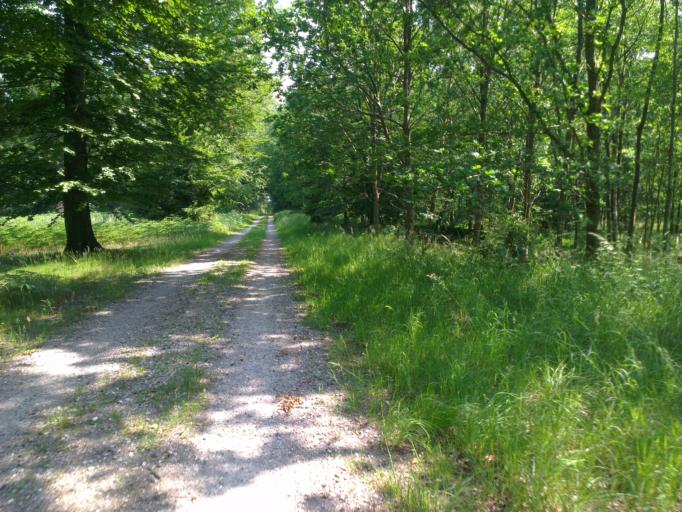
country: DK
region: Capital Region
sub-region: Allerod Kommune
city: Lillerod
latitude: 55.9143
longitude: 12.3622
